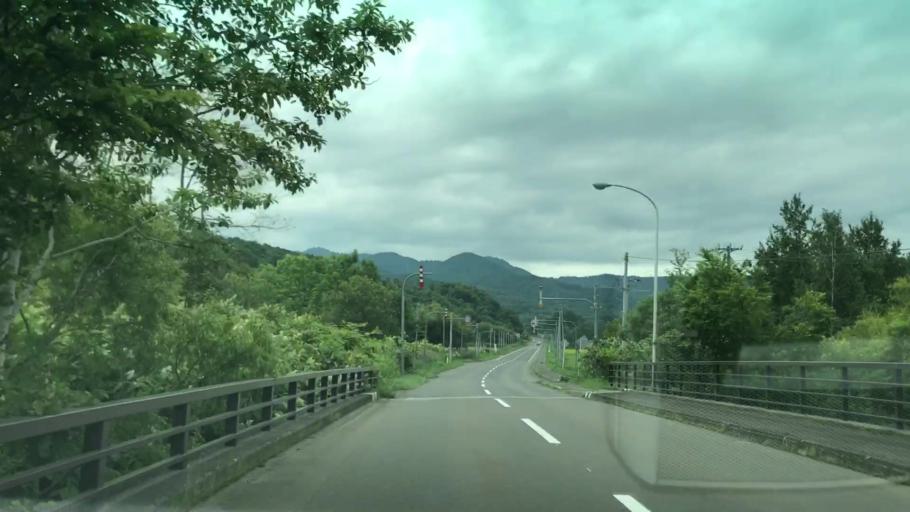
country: JP
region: Hokkaido
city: Yoichi
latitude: 43.0593
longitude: 140.8213
